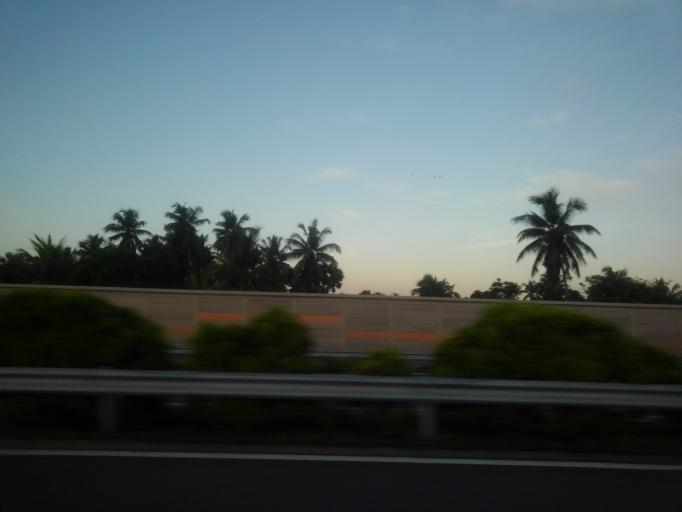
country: LK
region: Western
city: Hendala
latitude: 6.9993
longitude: 79.9045
